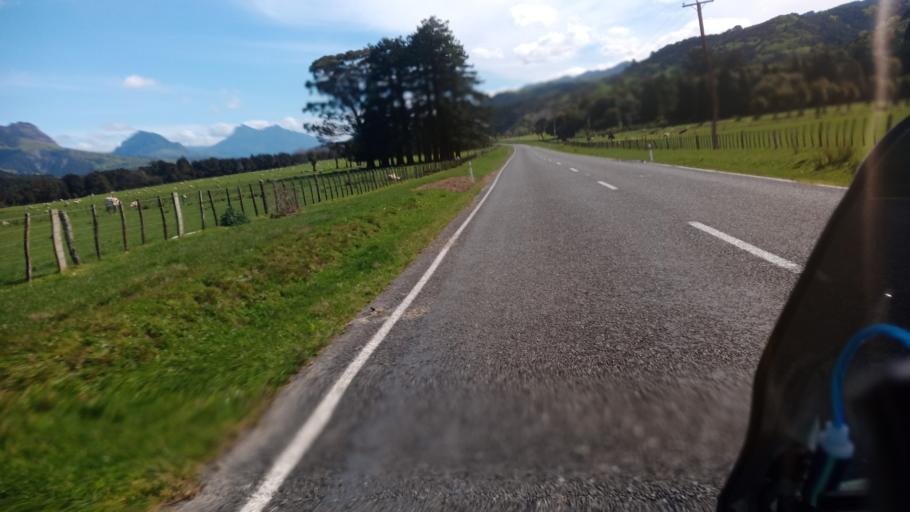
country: NZ
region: Gisborne
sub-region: Gisborne District
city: Gisborne
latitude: -37.8675
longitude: 178.2639
